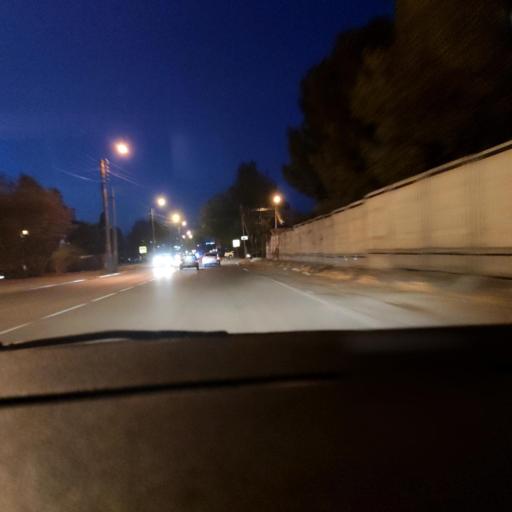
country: RU
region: Voronezj
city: Voronezh
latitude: 51.6294
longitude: 39.1755
